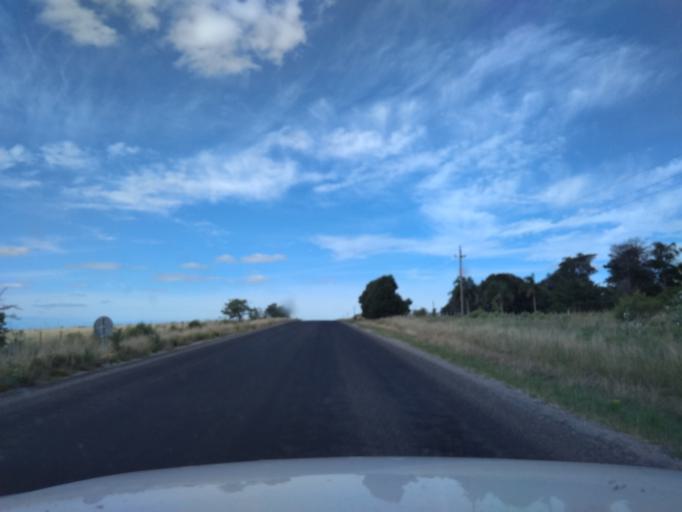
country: UY
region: Florida
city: Casupa
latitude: -34.0219
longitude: -55.8594
